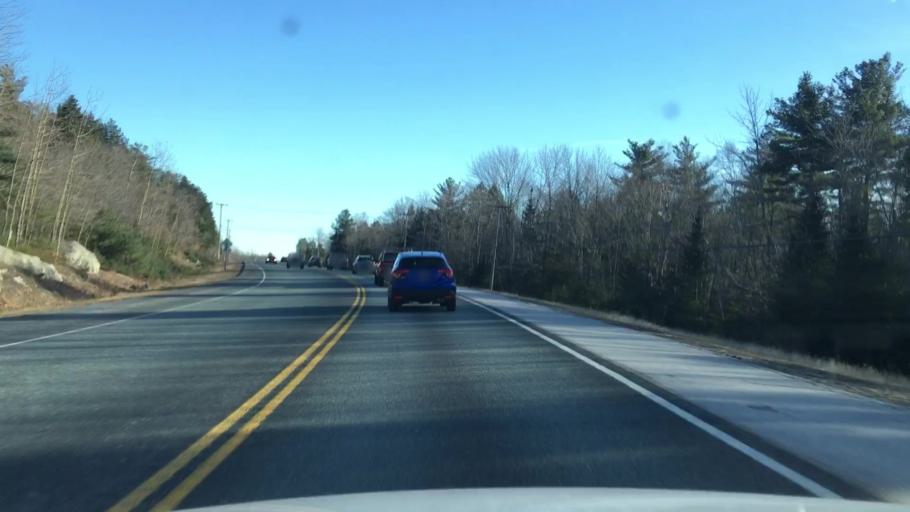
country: US
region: Maine
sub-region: Hancock County
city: Dedham
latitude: 44.6693
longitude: -68.5749
